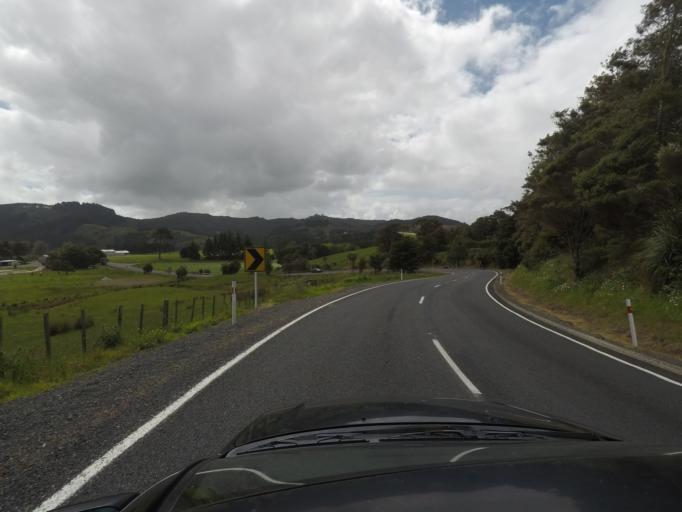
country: NZ
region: Auckland
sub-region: Auckland
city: Parakai
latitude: -36.5009
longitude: 174.5000
